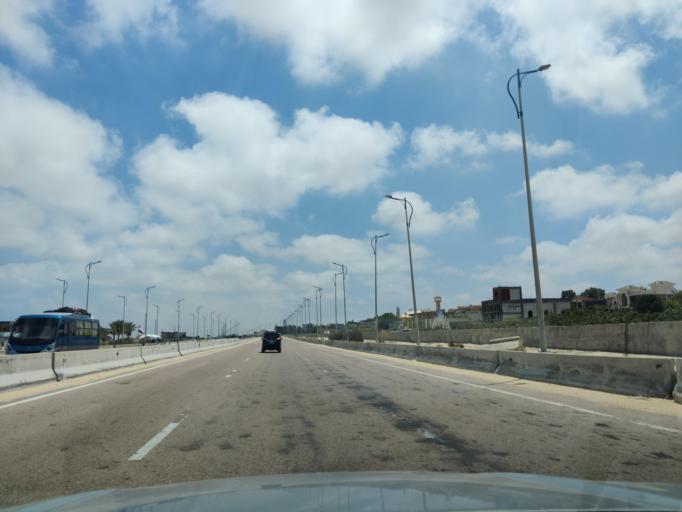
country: EG
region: Alexandria
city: Alexandria
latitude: 30.9678
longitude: 29.5577
